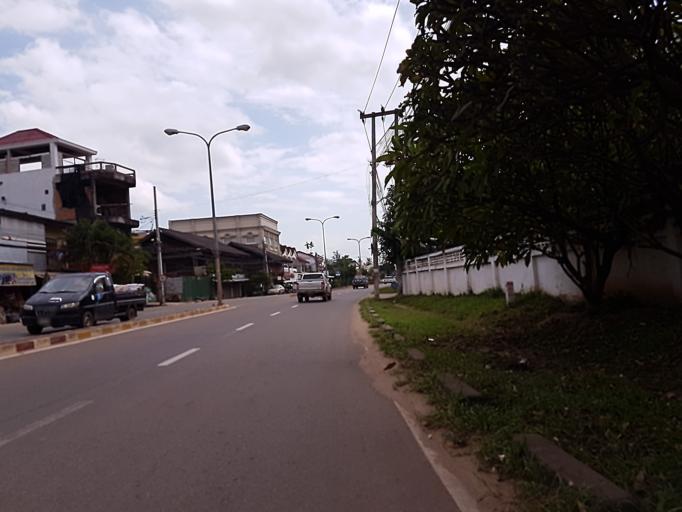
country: TH
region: Nong Khai
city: Si Chiang Mai
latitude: 17.9301
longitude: 102.6166
